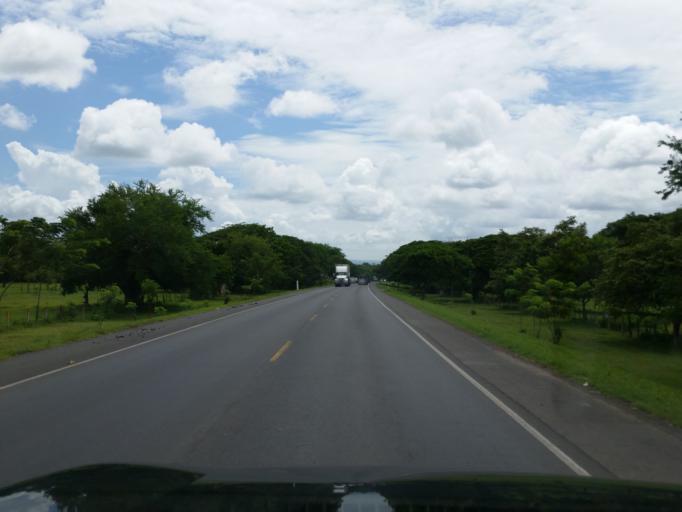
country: NI
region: Managua
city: Tipitapa
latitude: 12.1670
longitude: -86.1224
